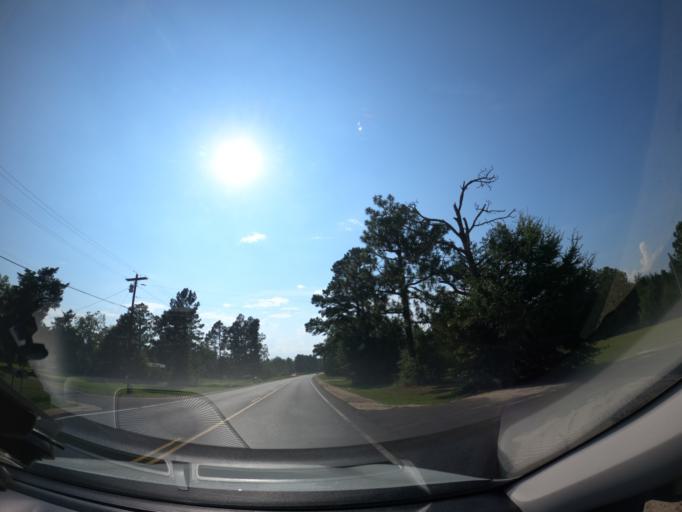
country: US
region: South Carolina
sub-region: Aiken County
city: New Ellenton
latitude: 33.3938
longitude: -81.7351
